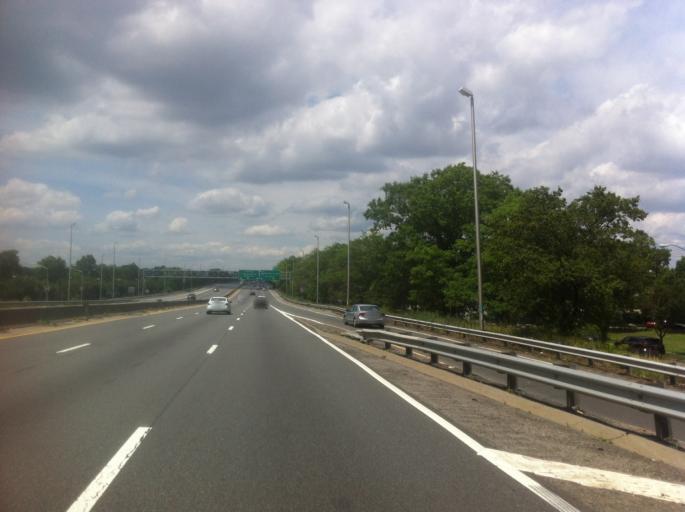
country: US
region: New York
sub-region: Bronx
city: The Bronx
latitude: 40.8254
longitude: -73.8266
